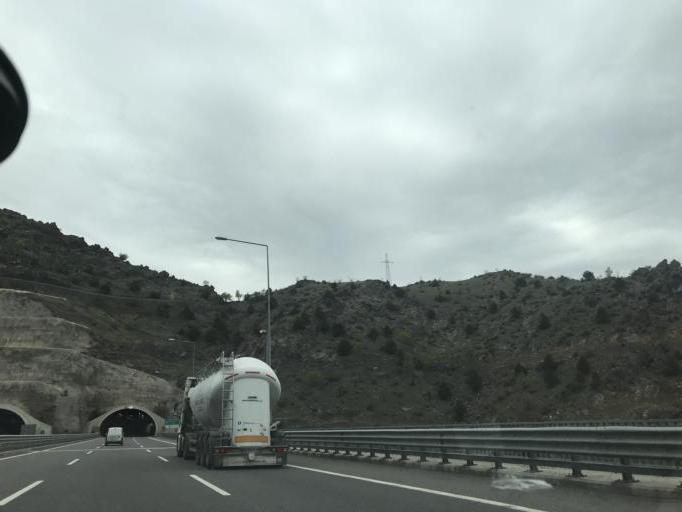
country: TR
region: Nigde
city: Ciftehan
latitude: 37.5570
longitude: 34.7664
